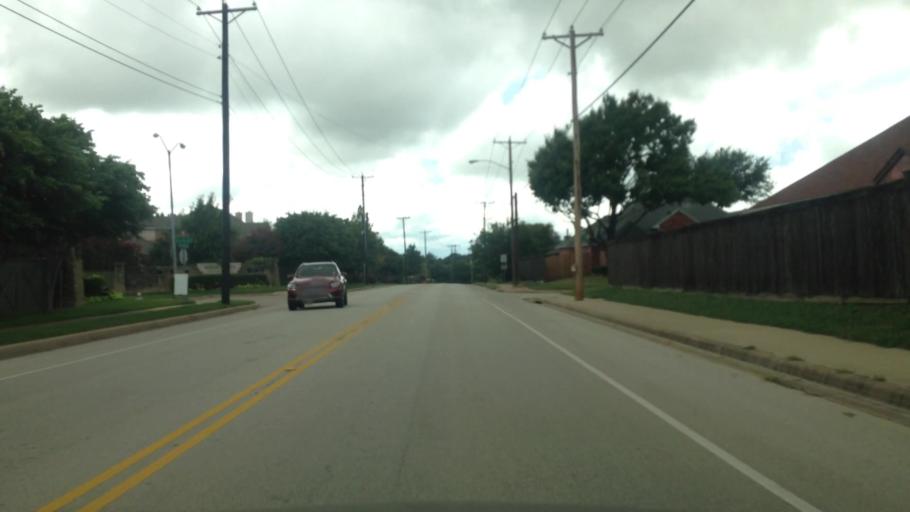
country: US
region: Texas
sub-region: Tarrant County
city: Crowley
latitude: 32.6281
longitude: -97.3977
